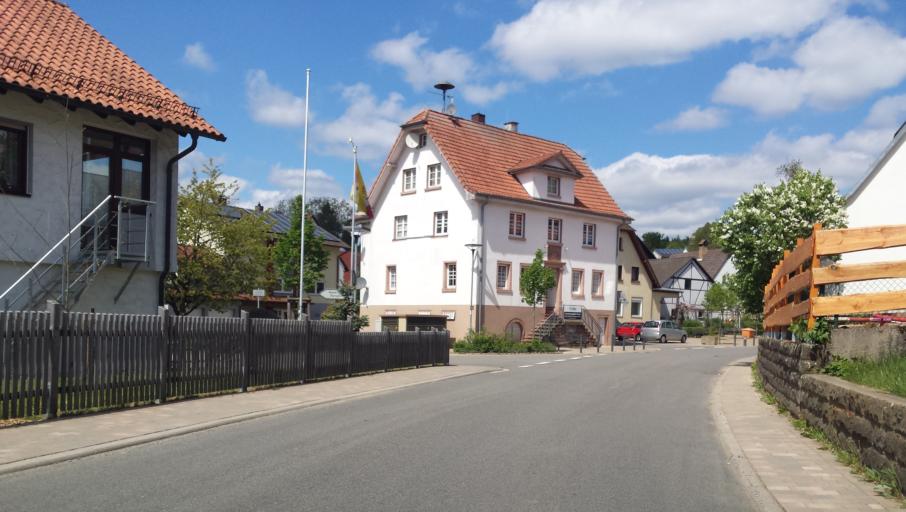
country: DE
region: Baden-Wuerttemberg
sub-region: Karlsruhe Region
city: Neunkirchen
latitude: 49.4010
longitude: 8.9741
